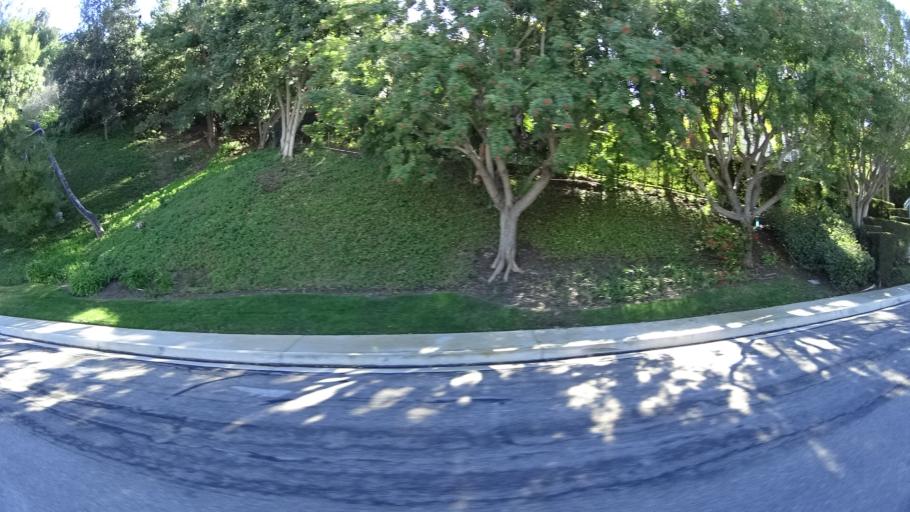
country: US
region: California
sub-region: Orange County
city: Villa Park
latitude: 33.8386
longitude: -117.8084
